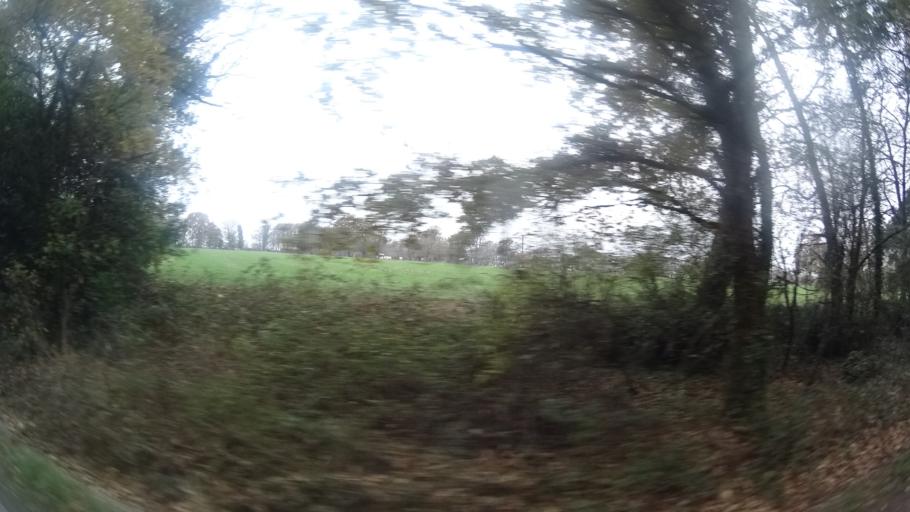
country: FR
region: Brittany
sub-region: Departement d'Ille-et-Vilaine
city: Bains-sur-Oust
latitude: 47.7051
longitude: -2.0550
